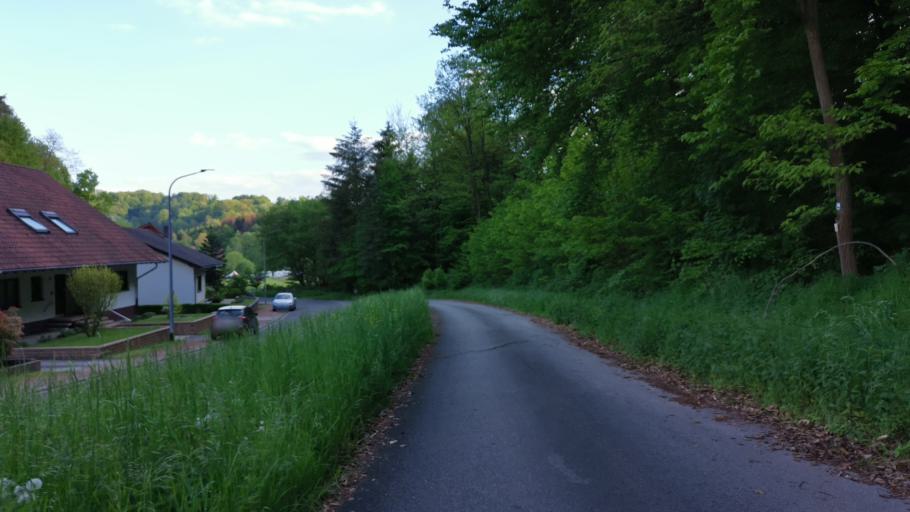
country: DE
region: Saarland
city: Kirkel
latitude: 49.2498
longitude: 7.1916
